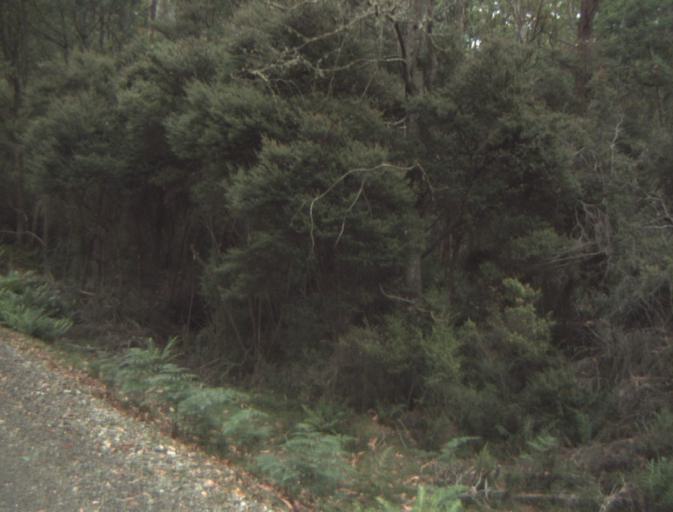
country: AU
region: Tasmania
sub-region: Dorset
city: Scottsdale
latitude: -41.4239
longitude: 147.5140
